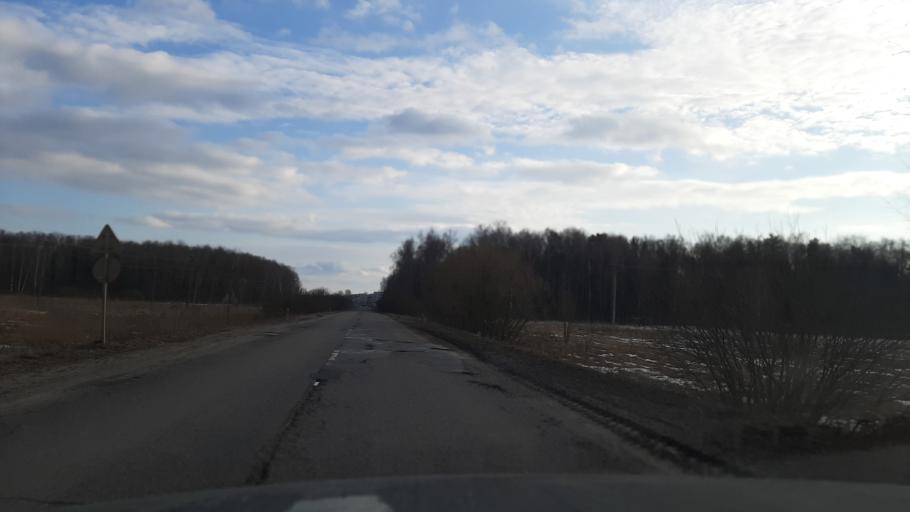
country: RU
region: Ivanovo
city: Novo-Talitsy
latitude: 56.9324
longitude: 40.7345
